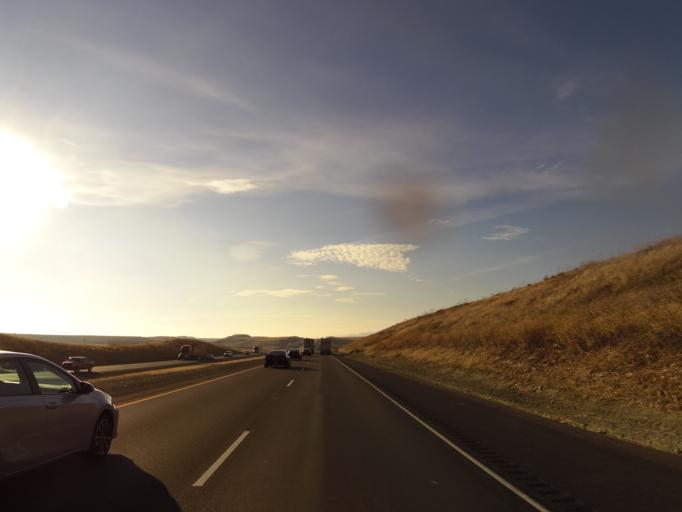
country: US
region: California
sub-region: Stanislaus County
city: Newman
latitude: 37.2755
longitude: -121.0966
